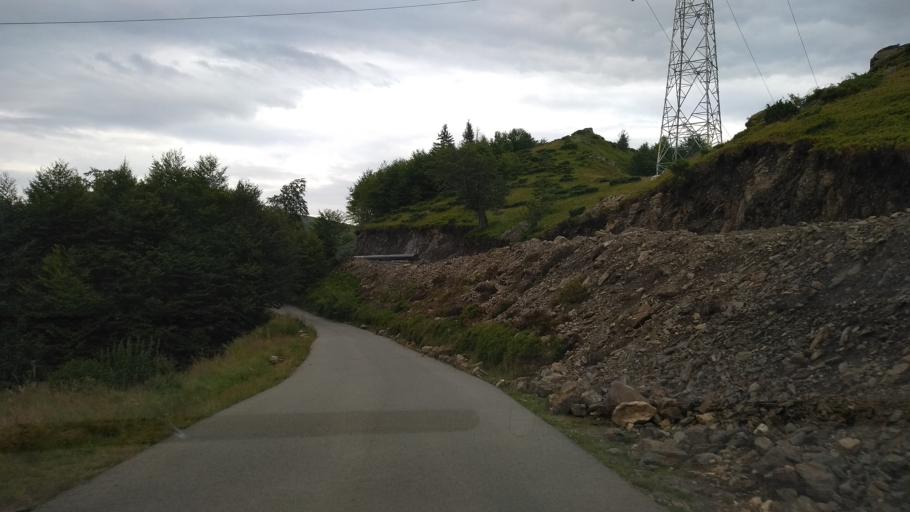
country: RO
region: Hunedoara
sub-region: Municipiul  Vulcan
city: Jiu-Paroseni
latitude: 45.3197
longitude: 23.2978
